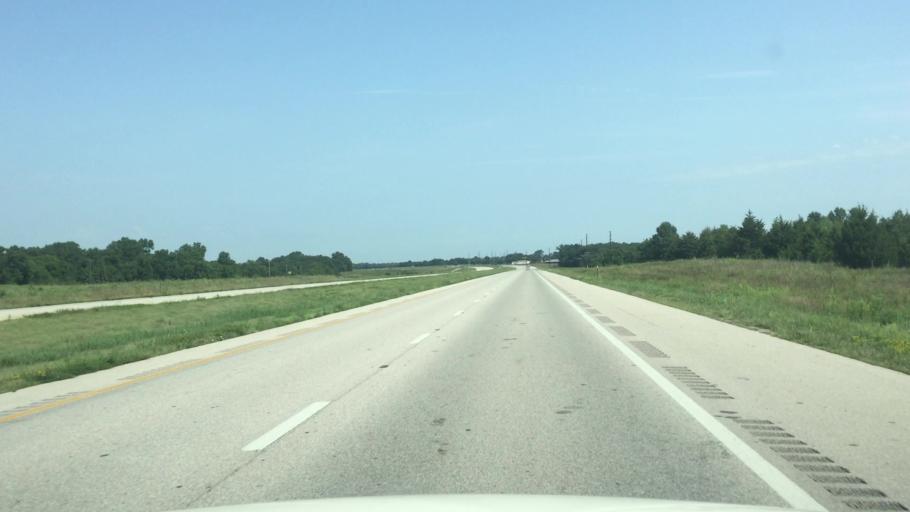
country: US
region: Kansas
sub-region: Montgomery County
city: Coffeyville
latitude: 37.0593
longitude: -95.5821
